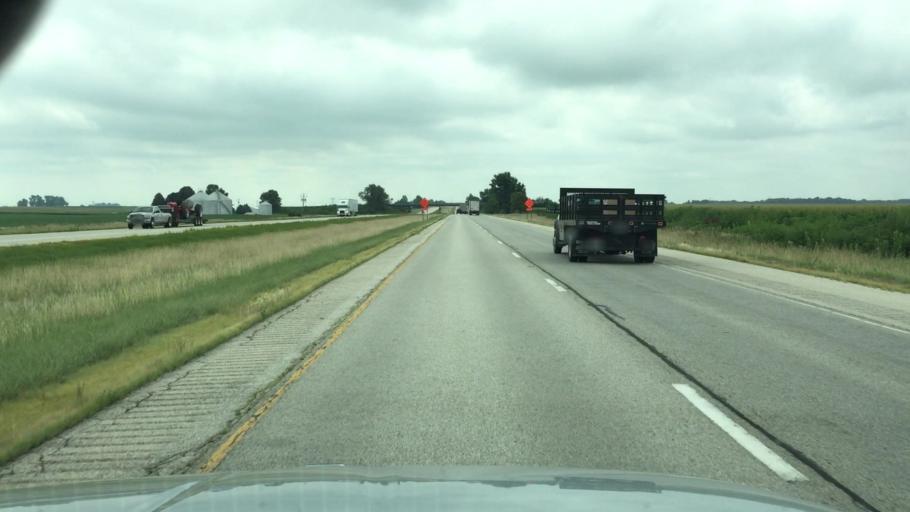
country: US
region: Illinois
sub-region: Knox County
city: Galesburg
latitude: 41.0399
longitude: -90.3345
